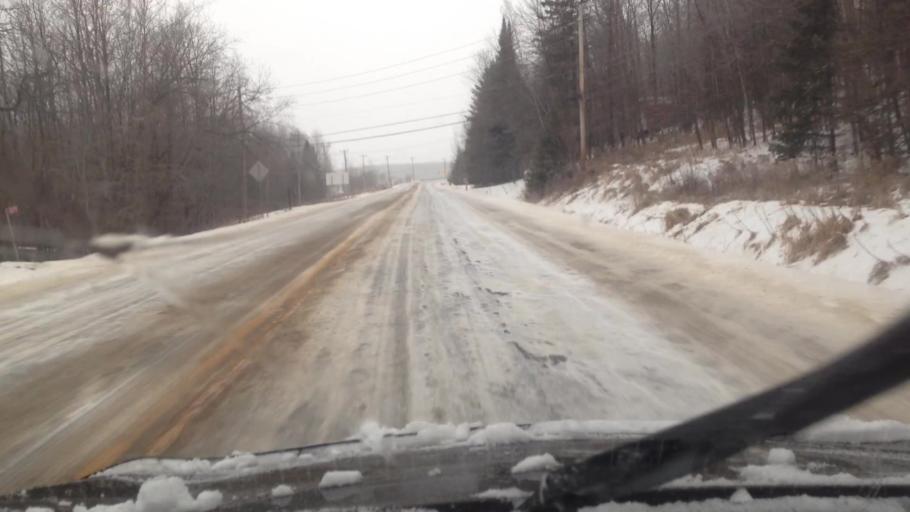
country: CA
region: Quebec
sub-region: Laurentides
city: Mont-Tremblant
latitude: 45.9475
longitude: -74.5598
